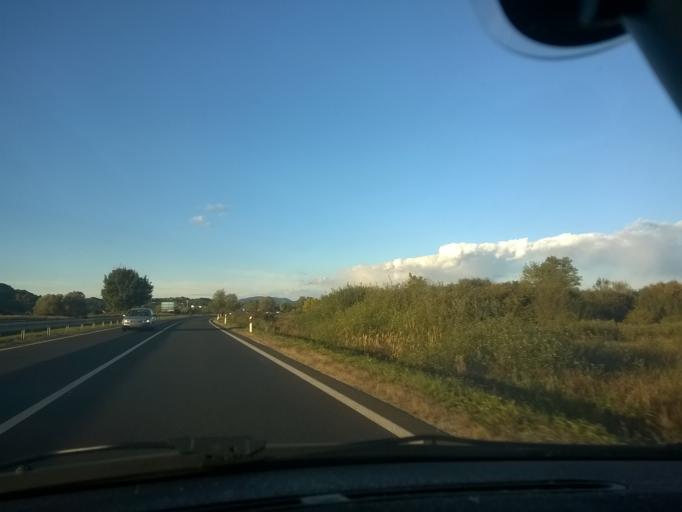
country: HR
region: Zagrebacka
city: Jakovlje
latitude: 45.9835
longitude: 15.8457
